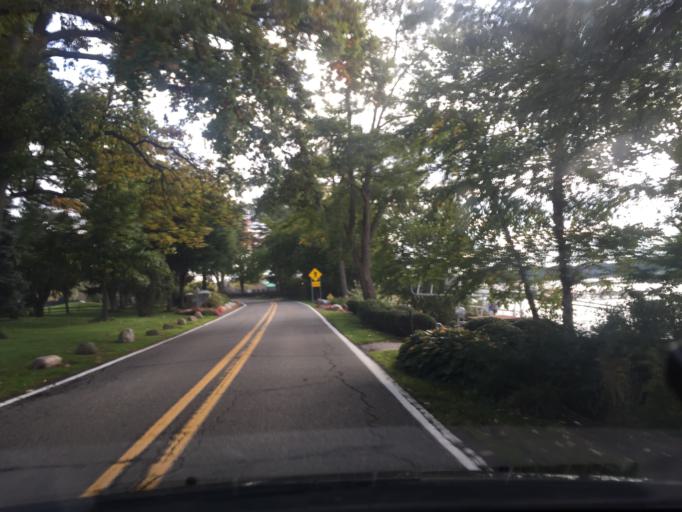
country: US
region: Michigan
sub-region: Oakland County
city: Keego Harbor
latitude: 42.5932
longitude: -83.3463
